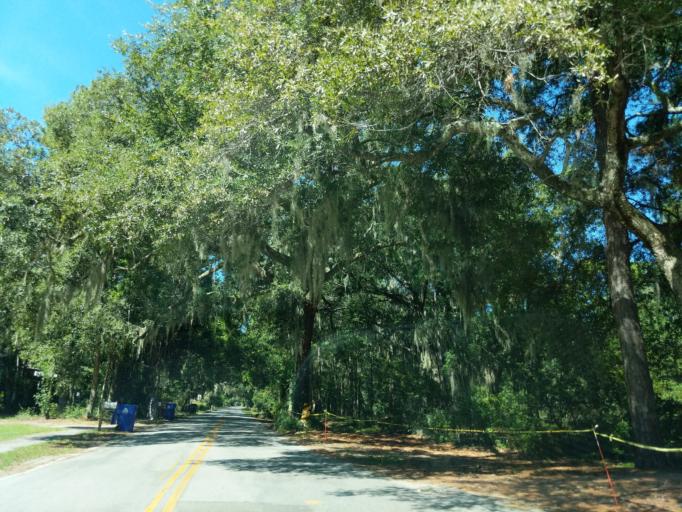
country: US
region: South Carolina
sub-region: Charleston County
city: Charleston
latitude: 32.7483
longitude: -79.9052
